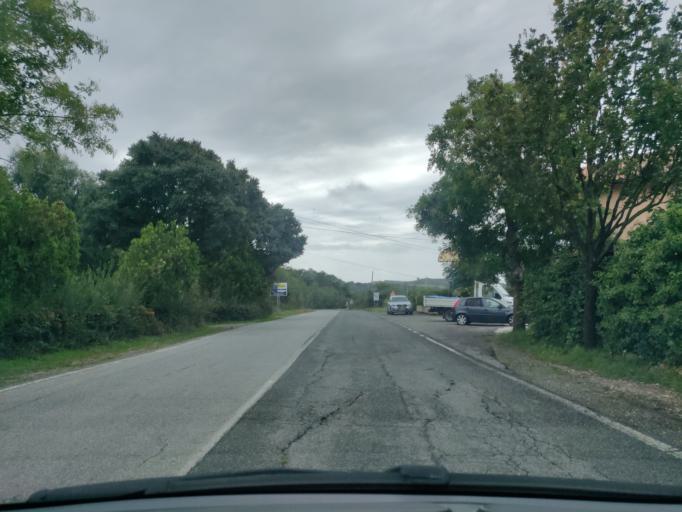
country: IT
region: Latium
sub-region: Citta metropolitana di Roma Capitale
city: Allumiere
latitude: 42.1256
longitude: 11.8644
